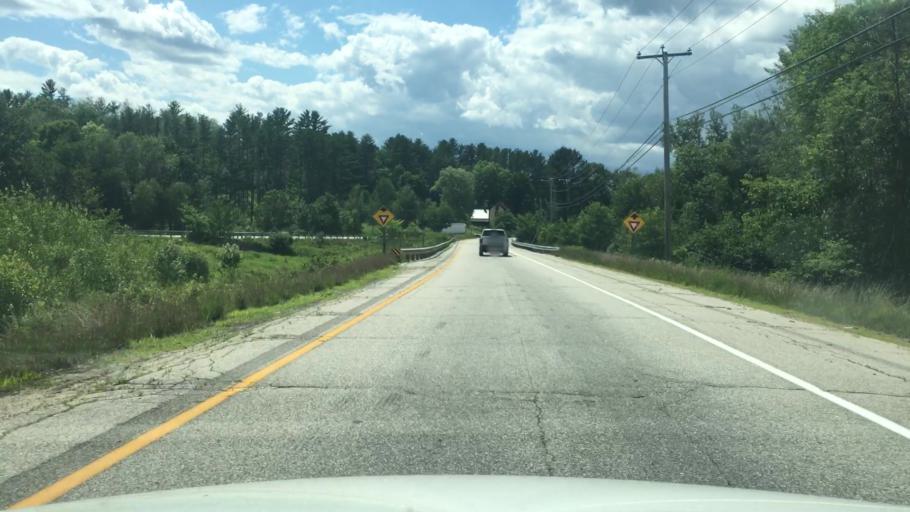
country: US
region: Maine
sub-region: Oxford County
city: Bethel
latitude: 44.4099
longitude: -70.7981
